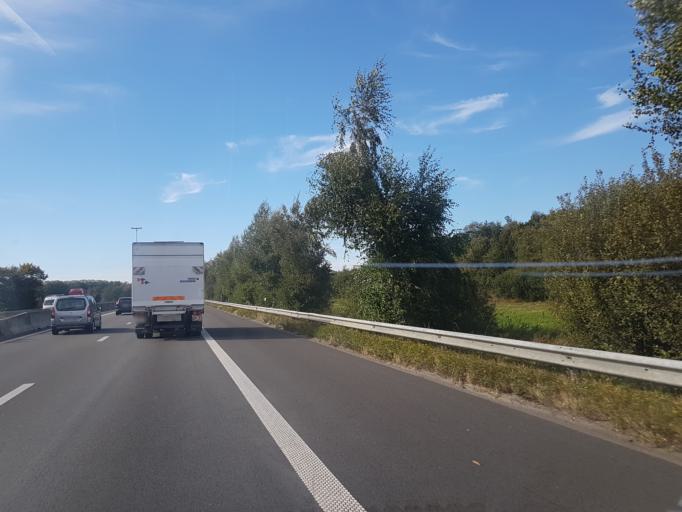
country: BE
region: Flanders
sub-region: Provincie Antwerpen
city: Nijlen
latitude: 51.1812
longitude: 4.6937
